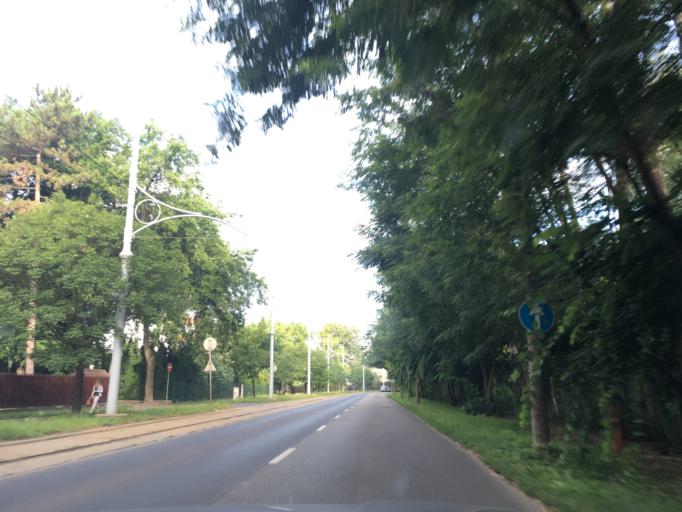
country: HU
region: Hajdu-Bihar
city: Debrecen
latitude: 47.5495
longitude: 21.6274
